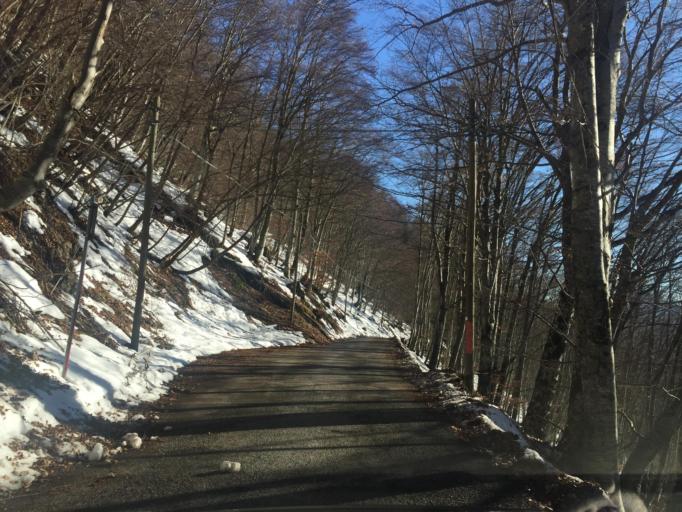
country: IT
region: Friuli Venezia Giulia
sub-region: Provincia di Udine
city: Lauco
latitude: 46.4506
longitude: 12.9293
